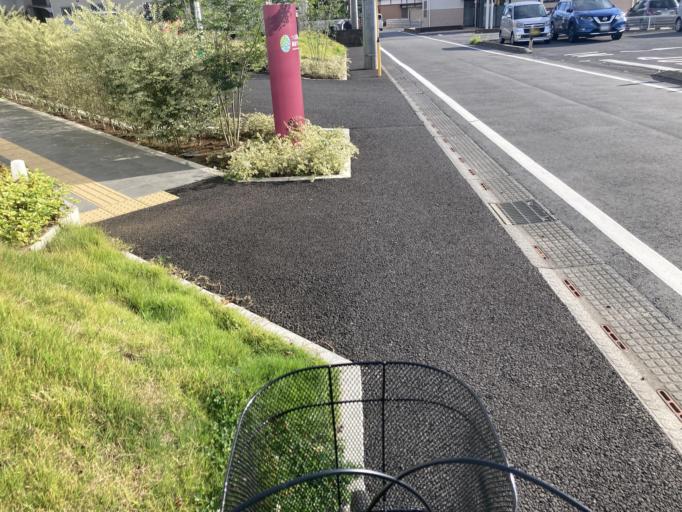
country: JP
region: Ibaraki
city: Naka
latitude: 36.0838
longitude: 140.0955
